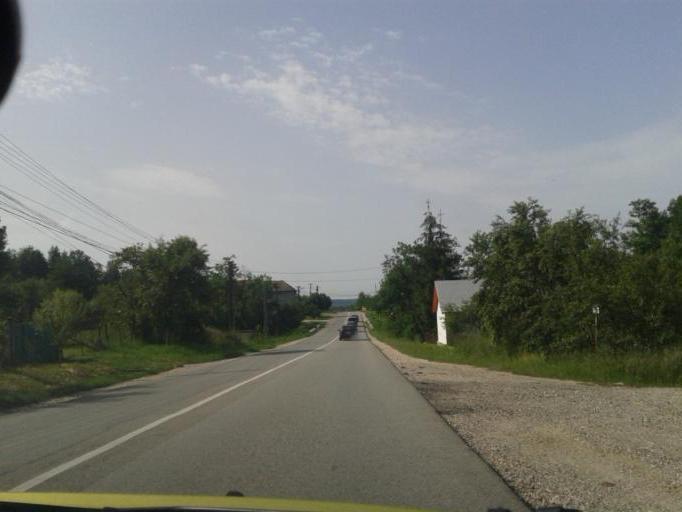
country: RO
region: Valcea
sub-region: Comuna Barbatesti
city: Bodesti
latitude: 45.1202
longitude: 24.1159
